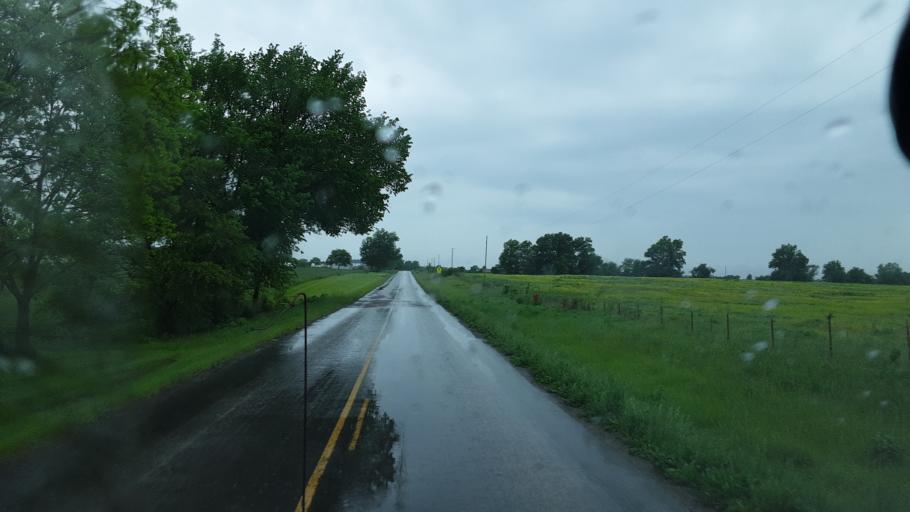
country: US
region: Missouri
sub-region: Randolph County
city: Moberly
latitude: 39.3679
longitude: -92.2549
